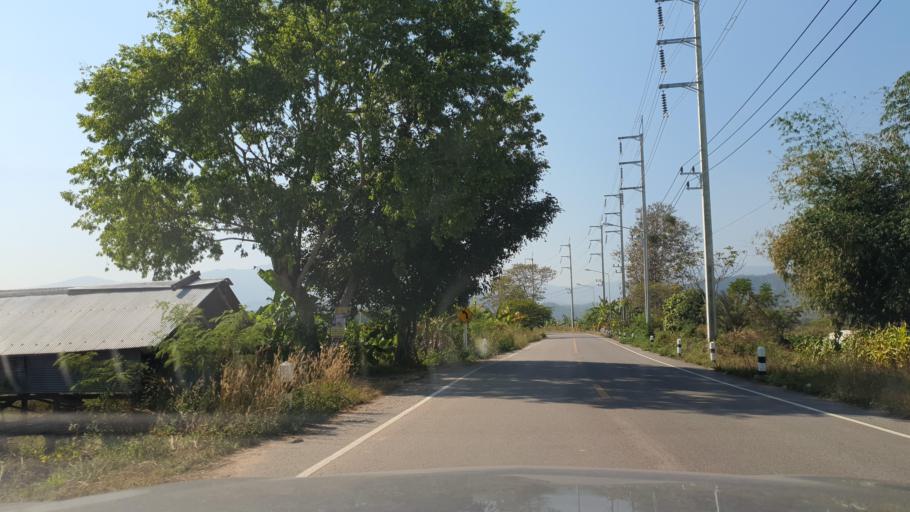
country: TH
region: Chiang Rai
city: Mae Lao
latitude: 19.8040
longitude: 99.6887
